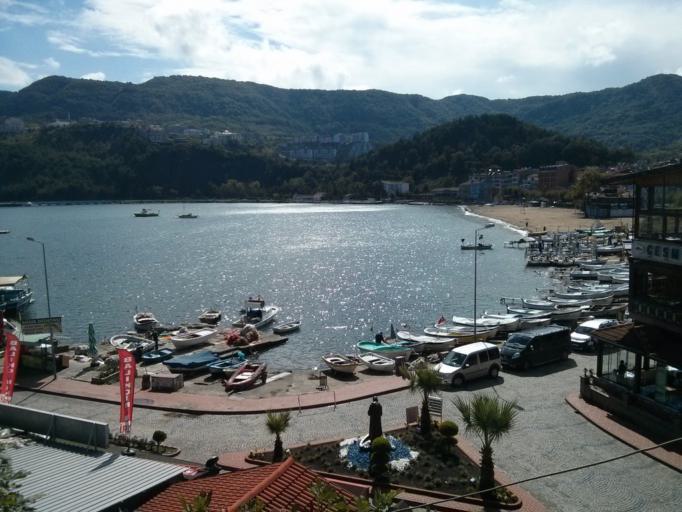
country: TR
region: Istanbul
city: Arikoey
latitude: 41.2442
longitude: 29.0323
